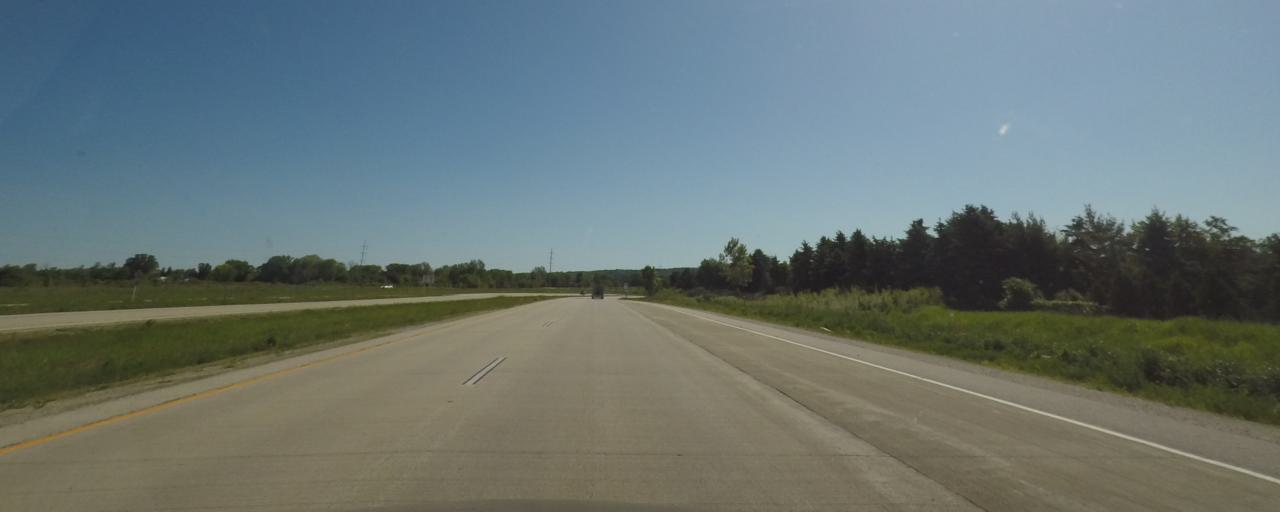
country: US
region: Wisconsin
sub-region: Fond du Lac County
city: Fond du Lac
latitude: 43.7447
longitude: -88.4150
